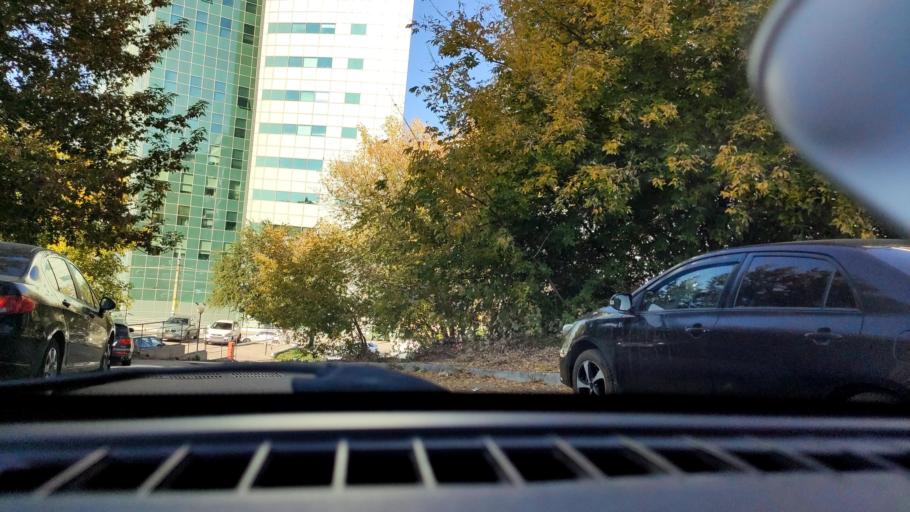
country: RU
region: Samara
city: Samara
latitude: 53.2108
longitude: 50.1241
